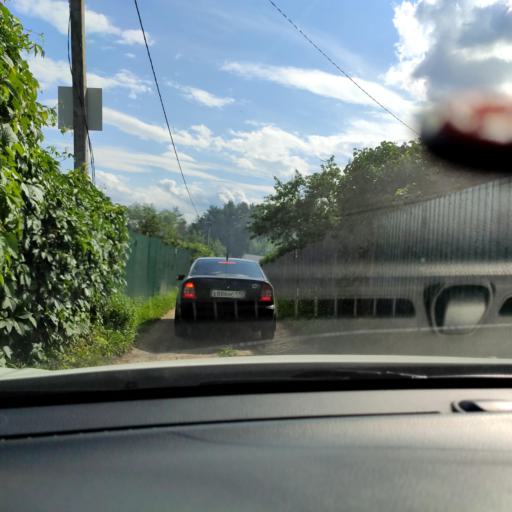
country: RU
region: Tatarstan
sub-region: Gorod Kazan'
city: Kazan
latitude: 55.8892
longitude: 49.0576
